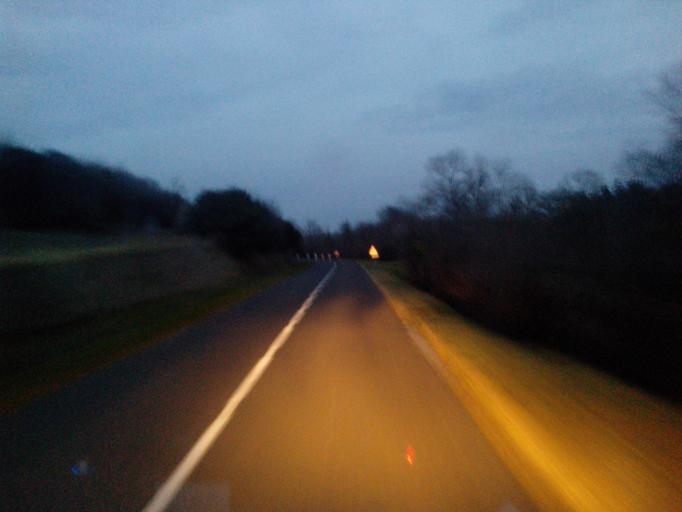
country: FR
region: Languedoc-Roussillon
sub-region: Departement de l'Aude
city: Villeneuve-la-Comptal
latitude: 43.2787
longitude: 1.8336
